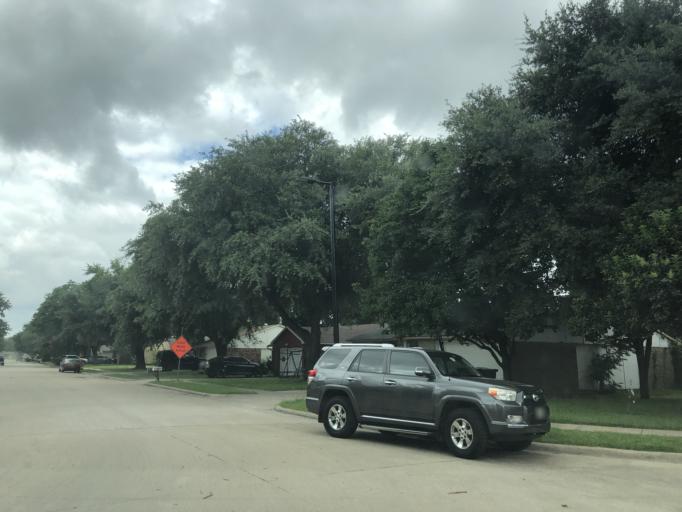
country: US
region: Texas
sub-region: Dallas County
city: Sunnyvale
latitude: 32.8467
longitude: -96.5677
